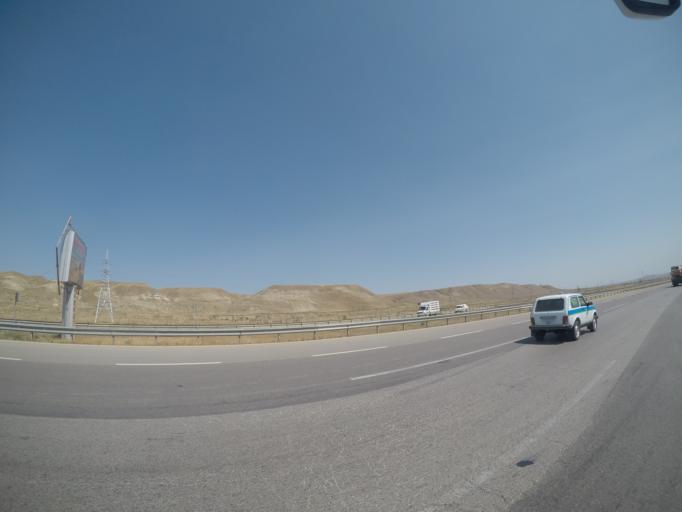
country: AZ
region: Haciqabul
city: Haciqabul
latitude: 40.0196
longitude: 48.9544
